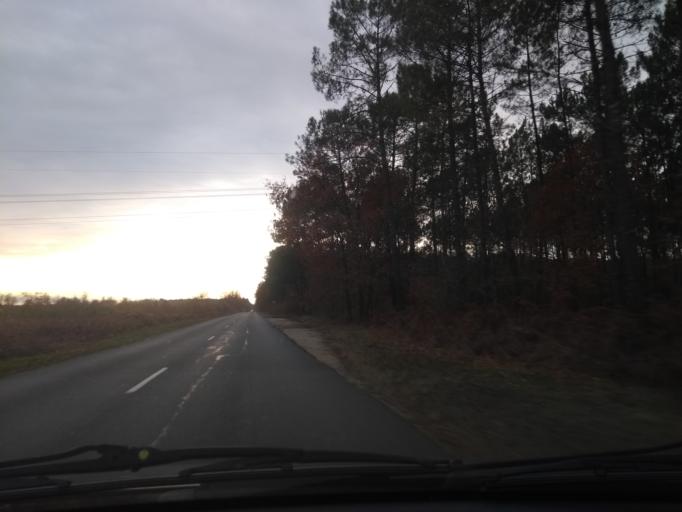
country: FR
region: Aquitaine
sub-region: Departement de la Gironde
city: Saucats
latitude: 44.6473
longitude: -0.6157
